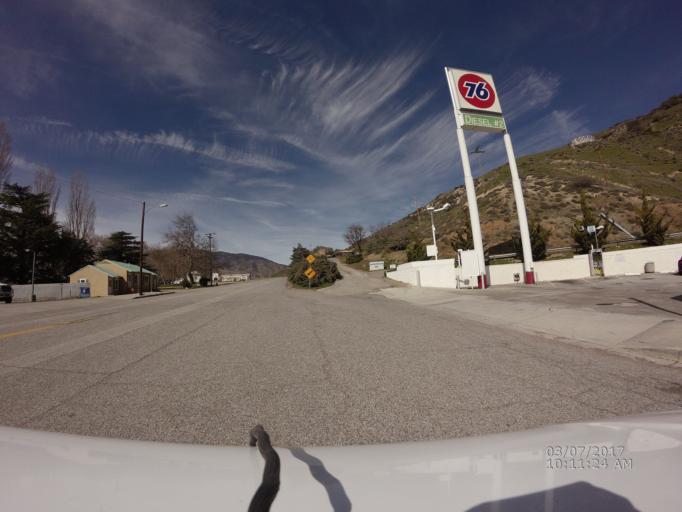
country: US
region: California
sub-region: Kern County
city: Lebec
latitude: 34.7966
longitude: -118.8533
